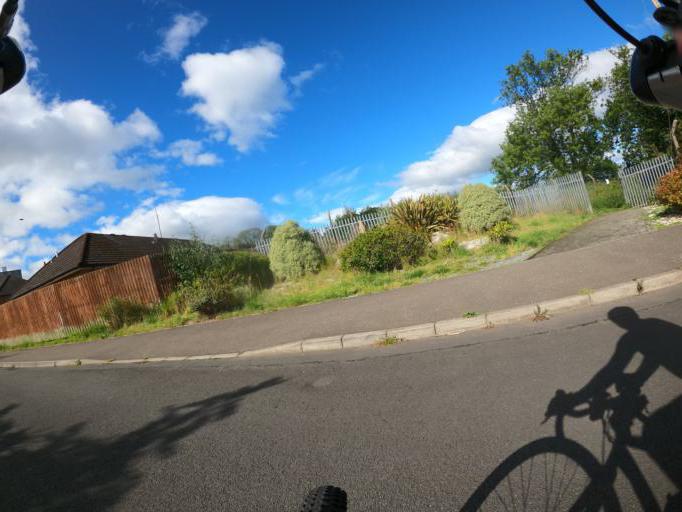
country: GB
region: Scotland
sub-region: Edinburgh
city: Edinburgh
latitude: 55.9751
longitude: -3.2598
